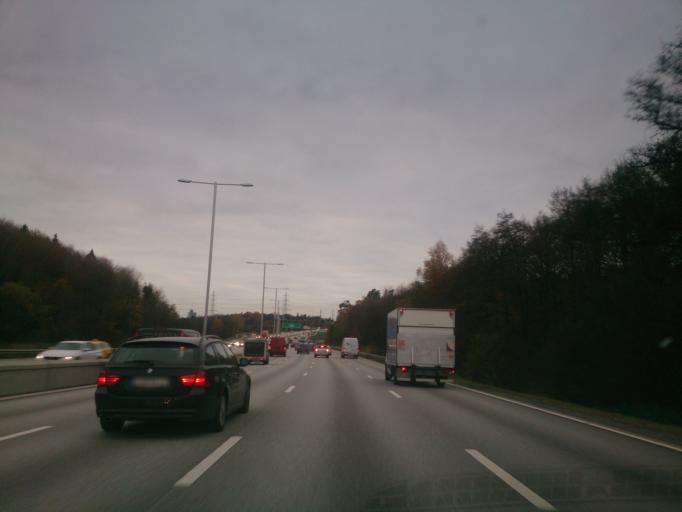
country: SE
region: Stockholm
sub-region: Solna Kommun
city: Rasunda
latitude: 59.3899
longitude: 17.9975
